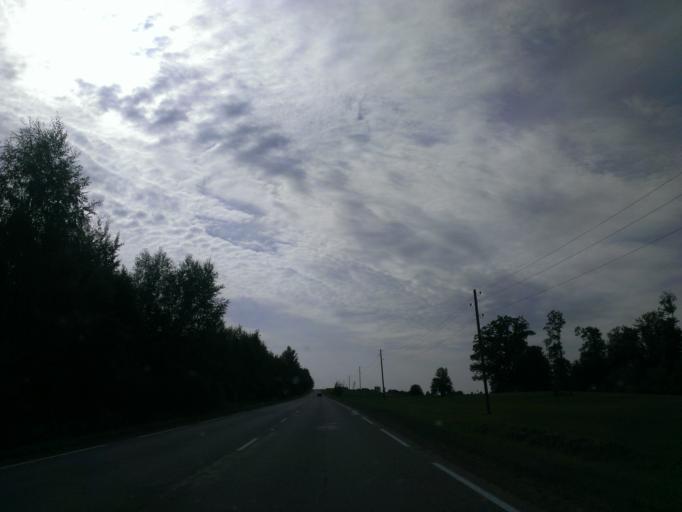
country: LV
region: Sigulda
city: Sigulda
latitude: 57.1772
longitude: 24.8193
